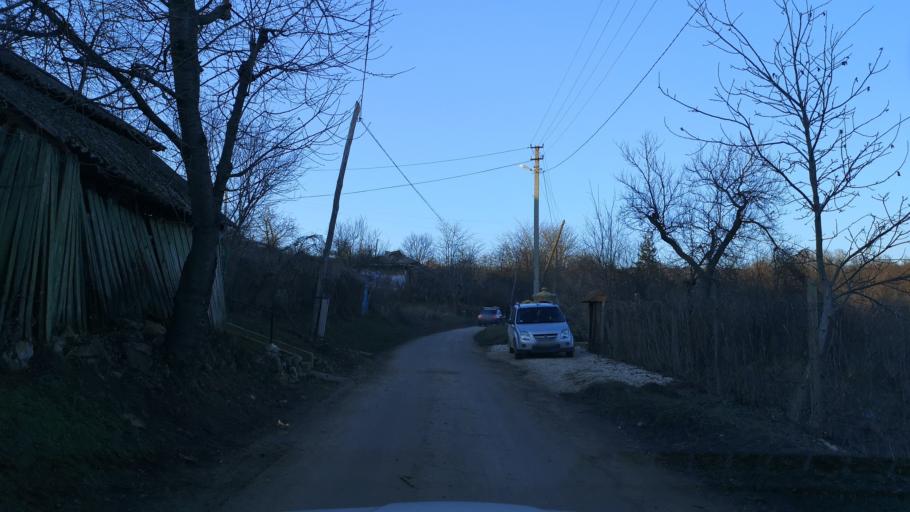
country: MD
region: Orhei
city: Orhei
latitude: 47.3665
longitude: 28.6903
